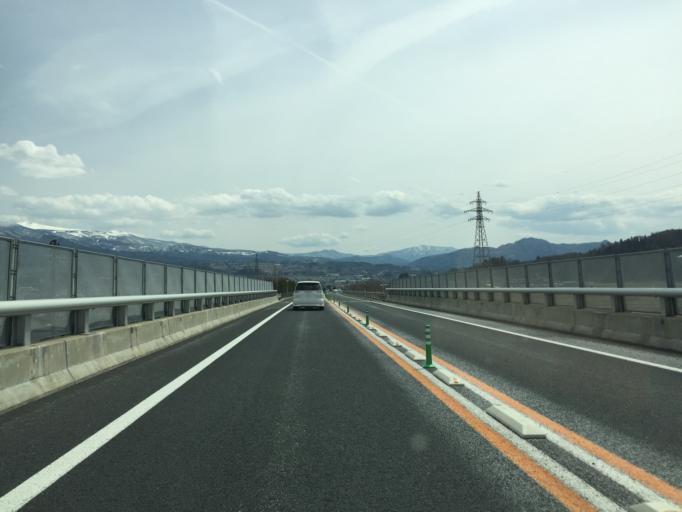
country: JP
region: Yamagata
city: Kaminoyama
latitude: 38.2143
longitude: 140.2888
